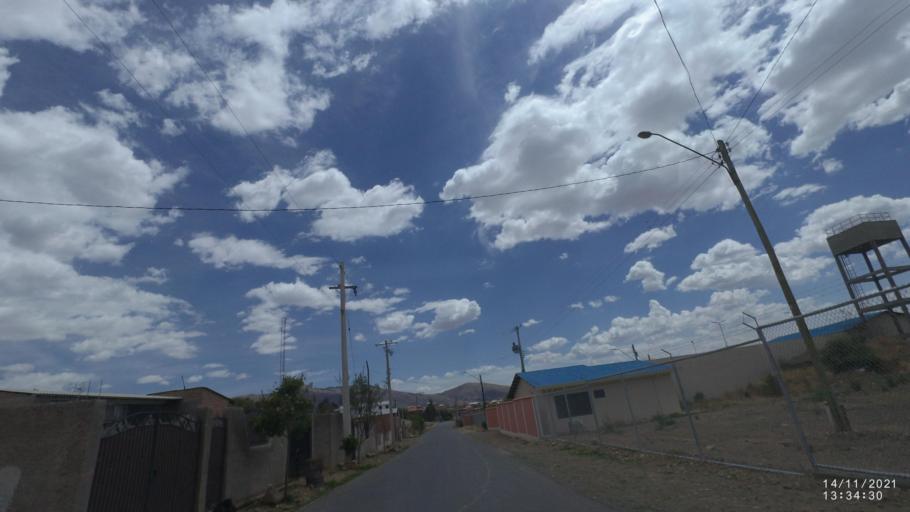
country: BO
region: Cochabamba
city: Colomi
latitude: -17.4028
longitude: -65.9846
